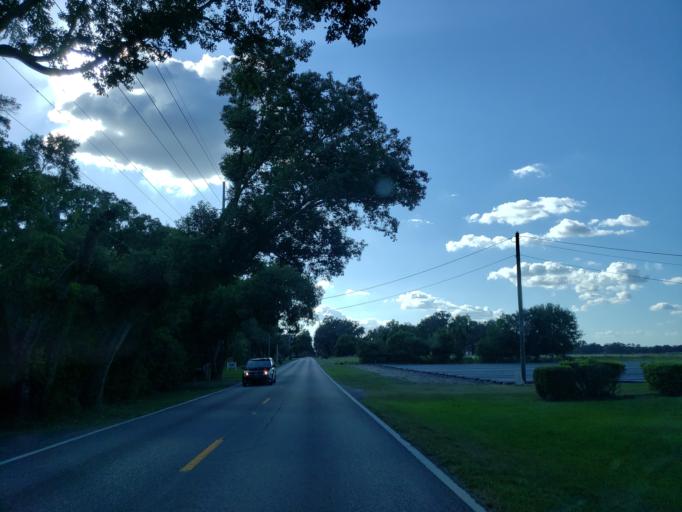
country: US
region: Florida
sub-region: Hillsborough County
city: Dover
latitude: 27.9670
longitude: -82.2088
